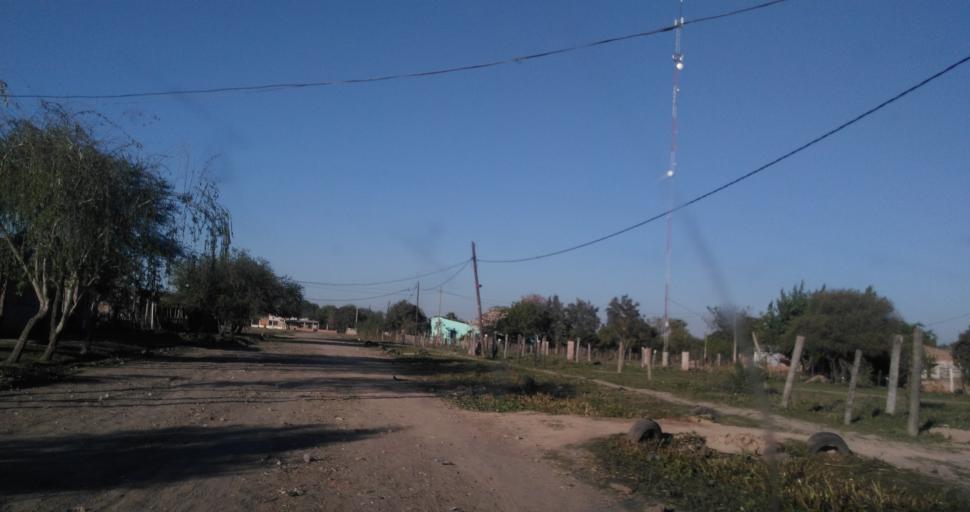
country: AR
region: Chaco
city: Resistencia
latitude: -27.4858
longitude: -58.9984
